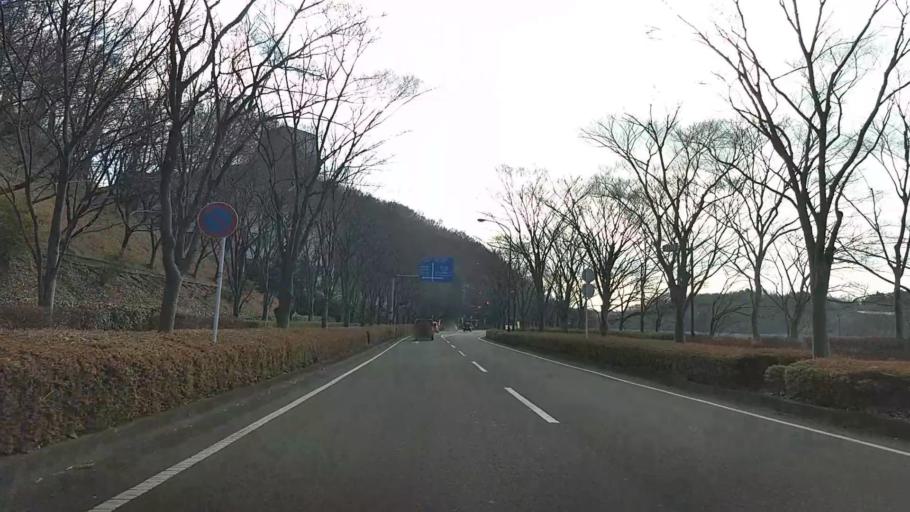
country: JP
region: Kanagawa
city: Atsugi
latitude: 35.4431
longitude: 139.3117
